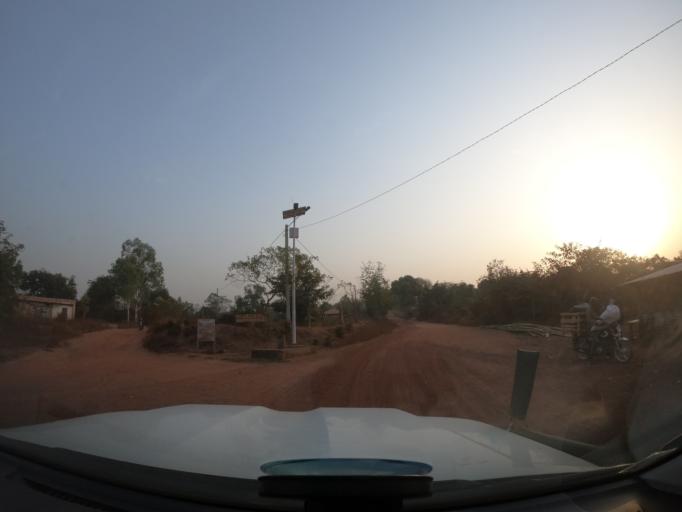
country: GN
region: Mamou
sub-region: Dalaba
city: Dalaba
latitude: 10.8777
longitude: -12.1822
